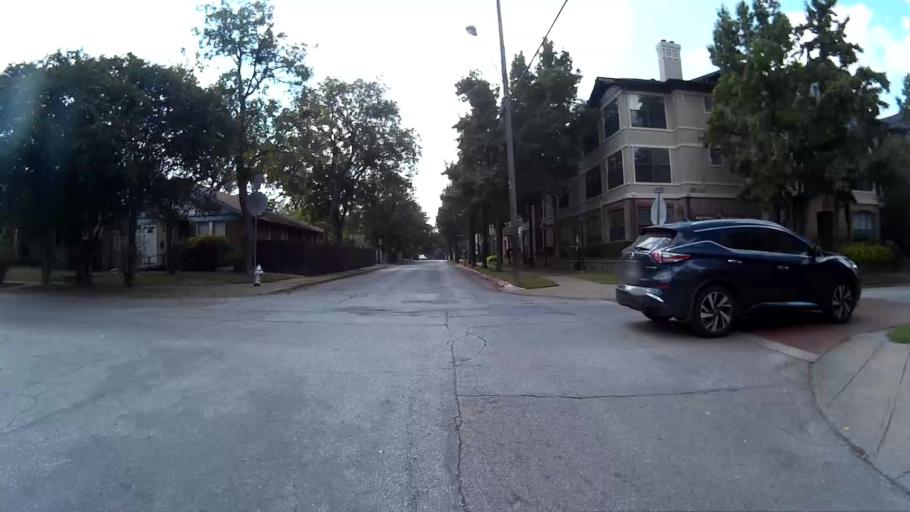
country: US
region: Texas
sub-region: Dallas County
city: Highland Park
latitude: 32.8203
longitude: -96.7824
